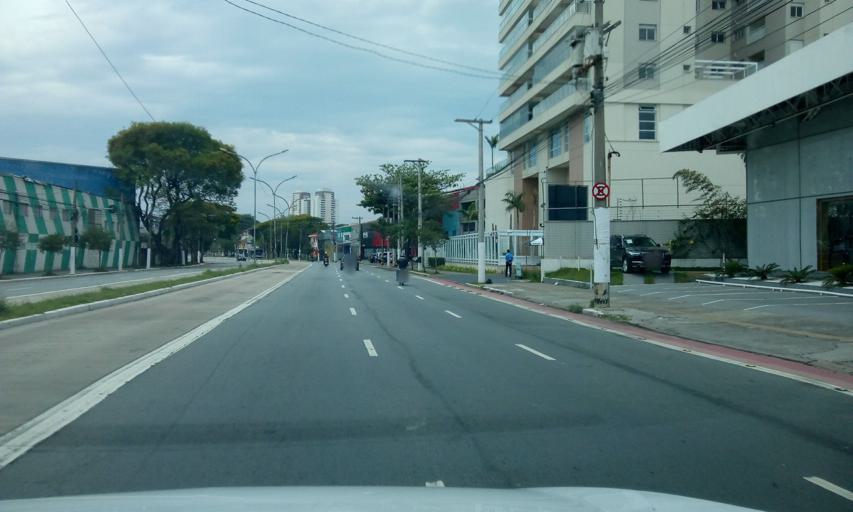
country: BR
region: Sao Paulo
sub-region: Sao Paulo
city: Sao Paulo
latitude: -23.5230
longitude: -46.6576
